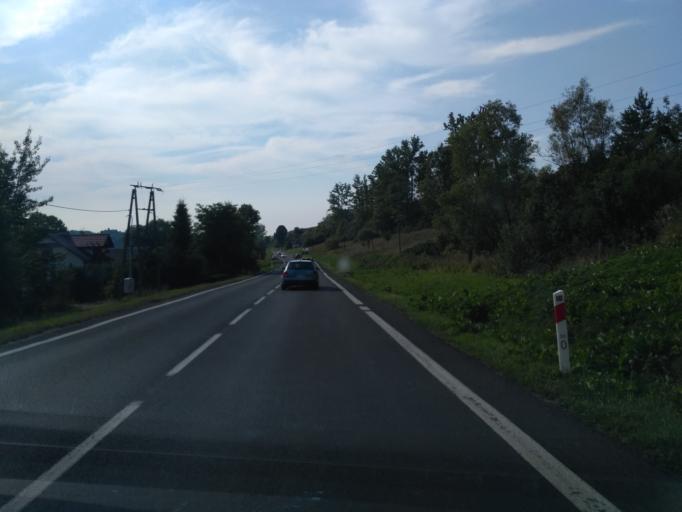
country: PL
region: Subcarpathian Voivodeship
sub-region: Powiat bieszczadzki
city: Ustrzyki Dolne
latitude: 49.4329
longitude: 22.5135
